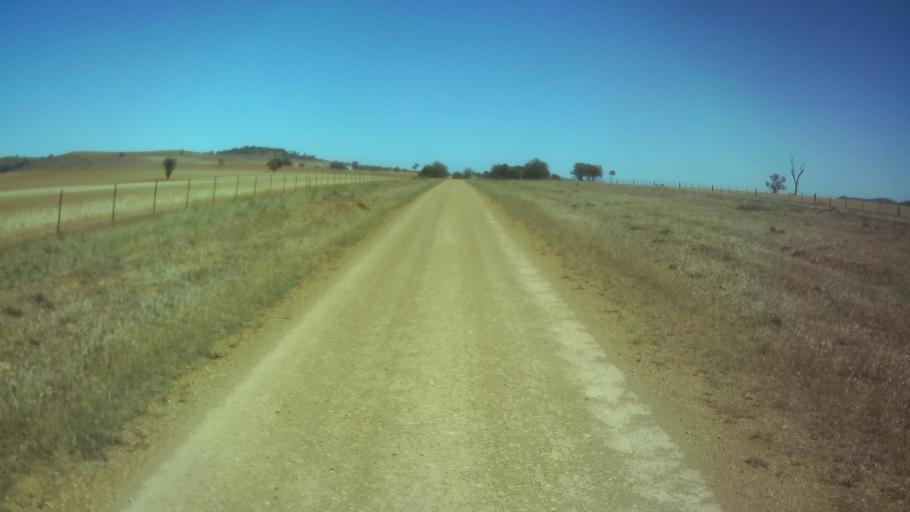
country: AU
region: New South Wales
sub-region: Weddin
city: Grenfell
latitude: -33.9659
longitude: 148.3109
